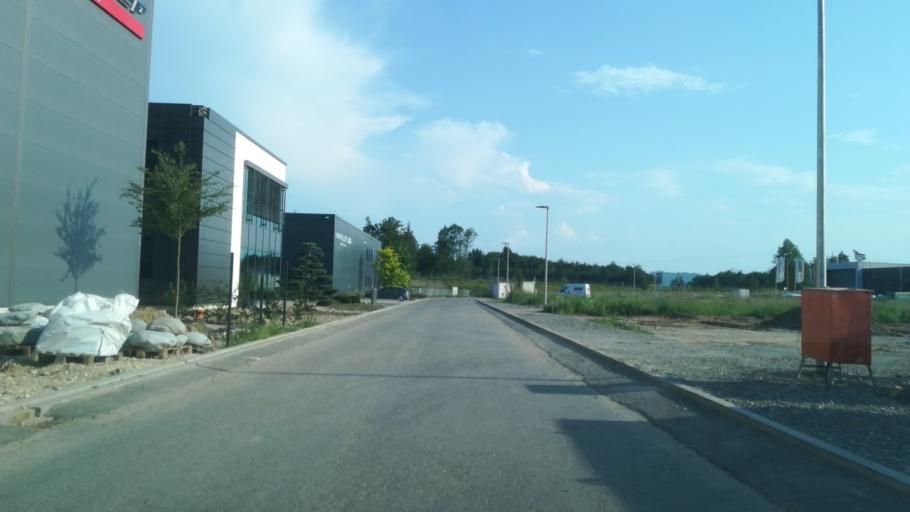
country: DE
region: Baden-Wuerttemberg
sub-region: Freiburg Region
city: Steisslingen
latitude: 47.7766
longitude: 8.9174
